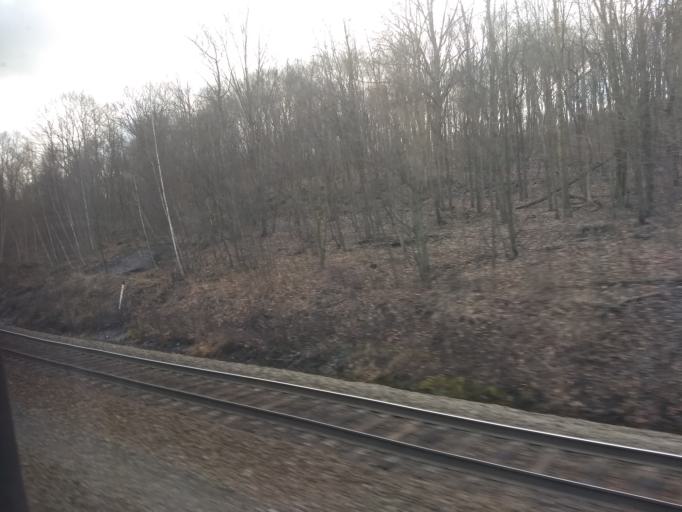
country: US
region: Pennsylvania
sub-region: Cambria County
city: Vinco
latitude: 40.3750
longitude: -78.8531
